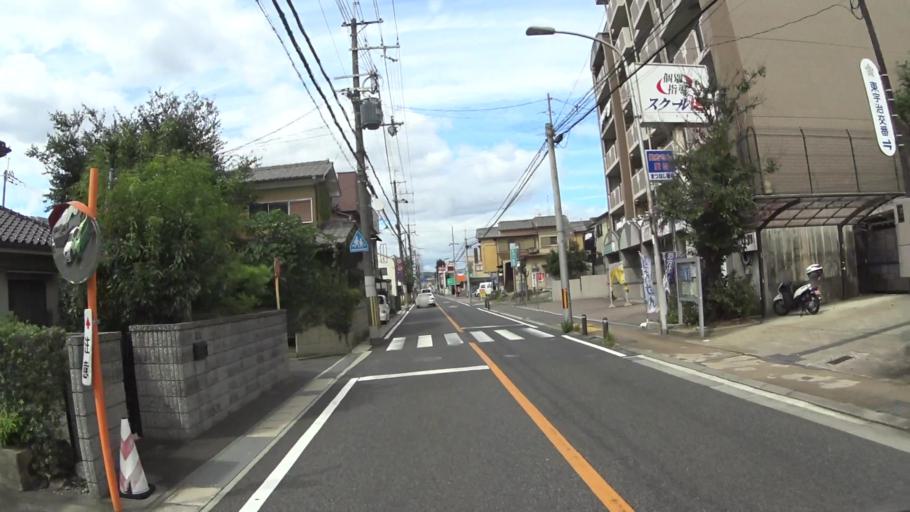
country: JP
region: Kyoto
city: Uji
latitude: 34.9094
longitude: 135.8053
